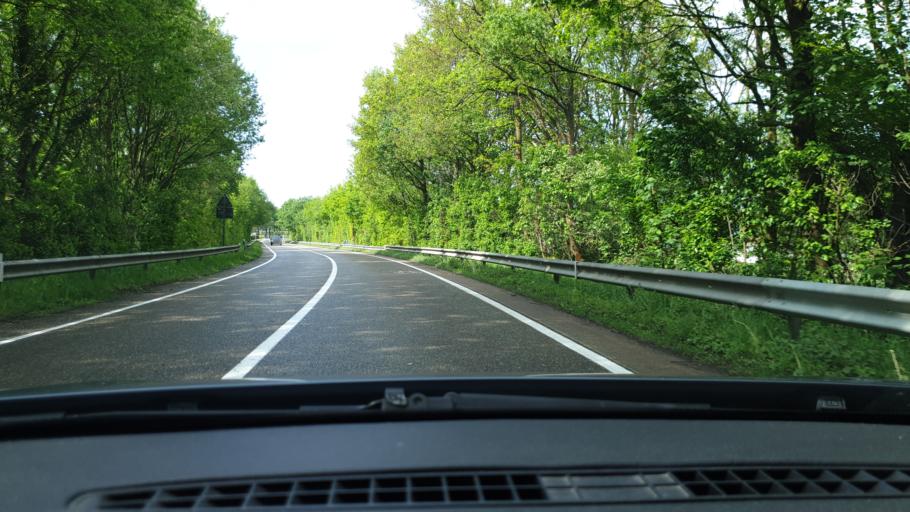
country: BE
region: Flanders
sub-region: Provincie Limburg
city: Tessenderlo
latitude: 51.1001
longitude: 5.1072
